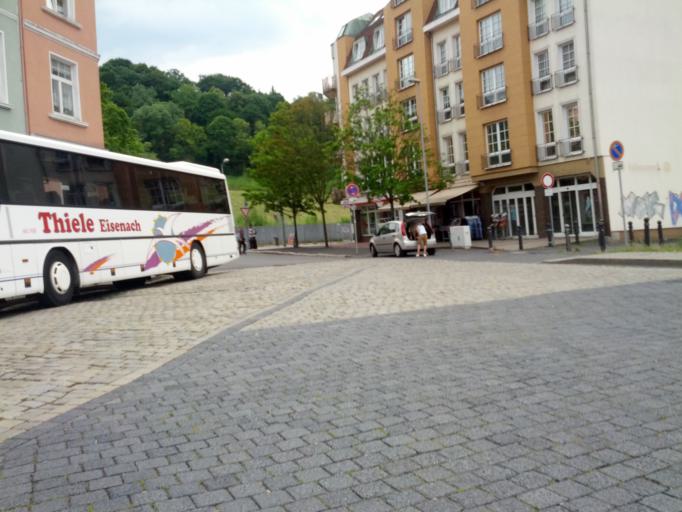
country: DE
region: Thuringia
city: Eisenach
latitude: 50.9768
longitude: 10.3292
